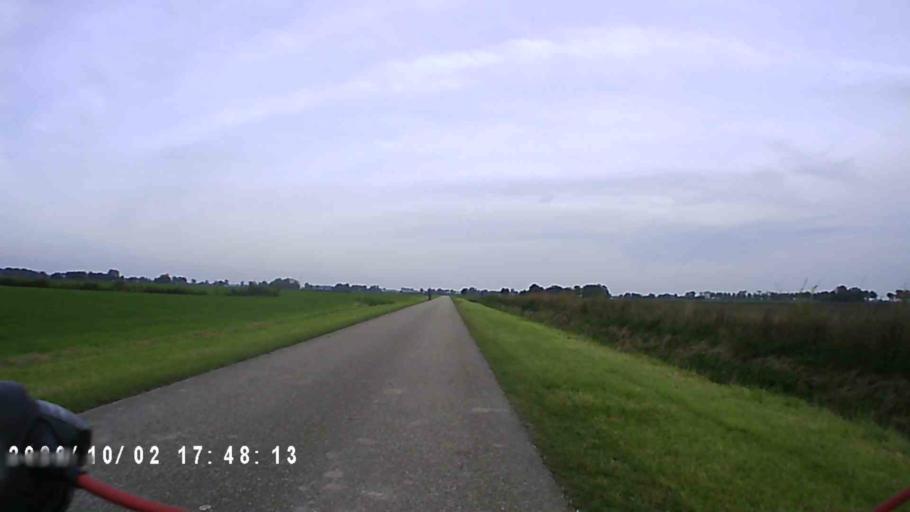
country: NL
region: Groningen
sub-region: Gemeente Zuidhorn
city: Oldehove
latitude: 53.3379
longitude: 6.3996
